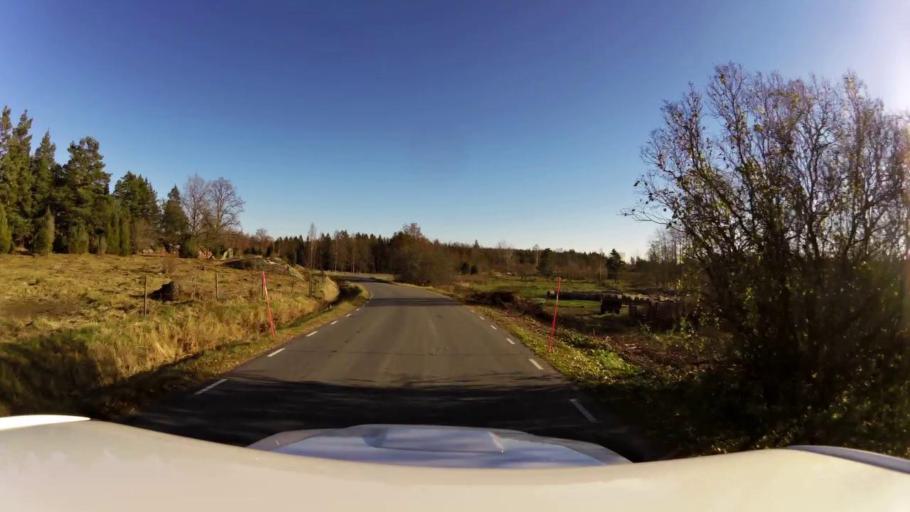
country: SE
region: OEstergoetland
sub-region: Linkopings Kommun
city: Sturefors
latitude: 58.2758
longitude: 15.6574
